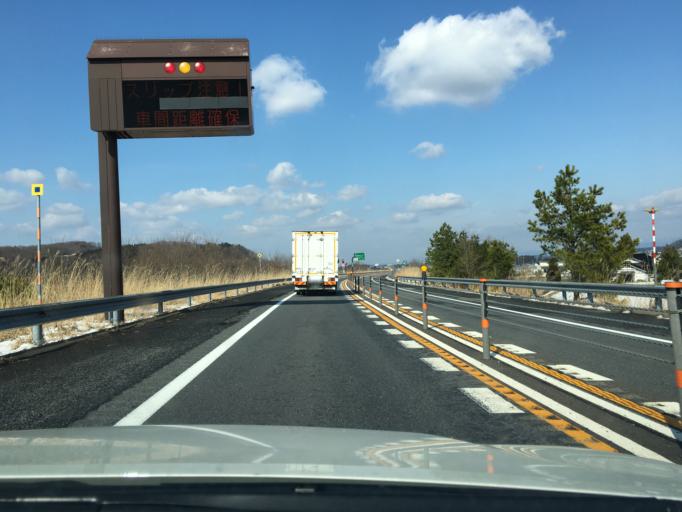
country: JP
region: Yamagata
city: Tsuruoka
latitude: 38.6128
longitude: 139.8420
